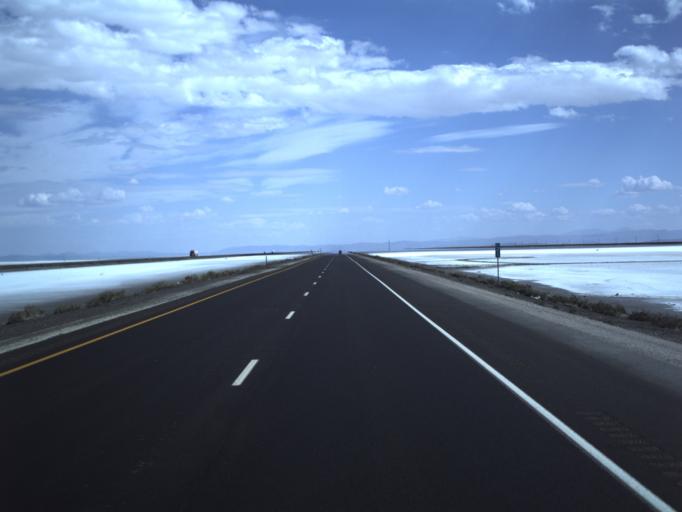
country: US
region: Utah
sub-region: Tooele County
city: Wendover
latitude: 40.7342
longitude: -113.6466
